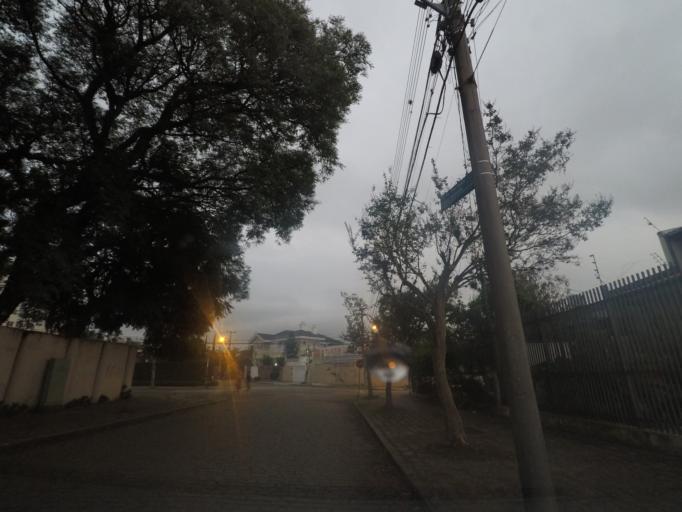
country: BR
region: Parana
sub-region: Curitiba
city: Curitiba
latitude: -25.4421
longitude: -49.2500
